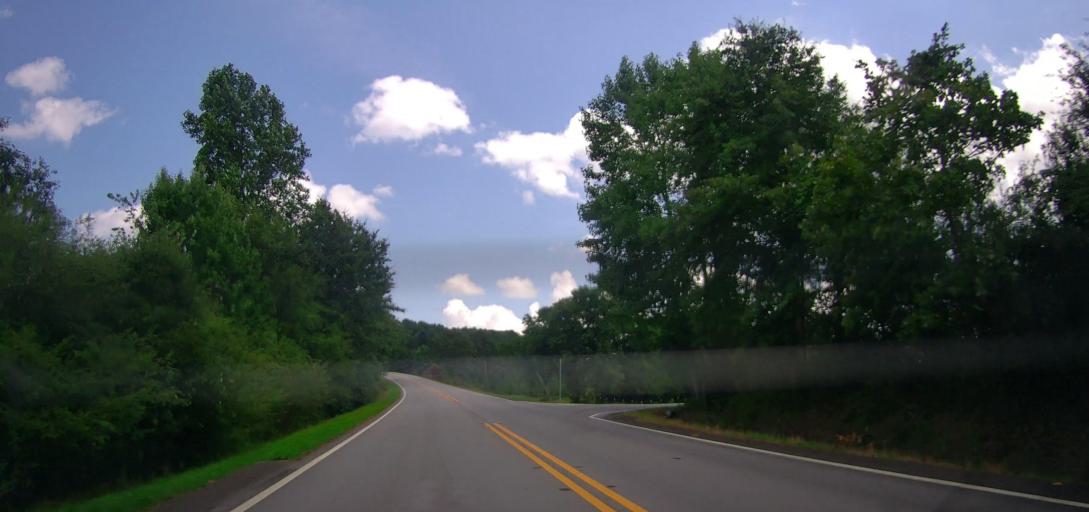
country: US
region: Georgia
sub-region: Carroll County
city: Bowdon
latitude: 33.4375
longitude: -85.2749
